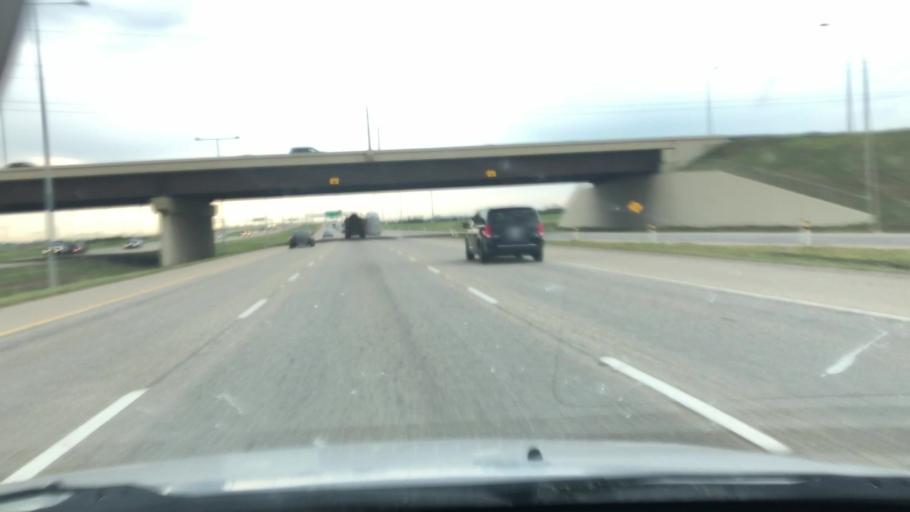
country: CA
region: Alberta
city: Beaumont
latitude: 53.4375
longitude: -113.4651
